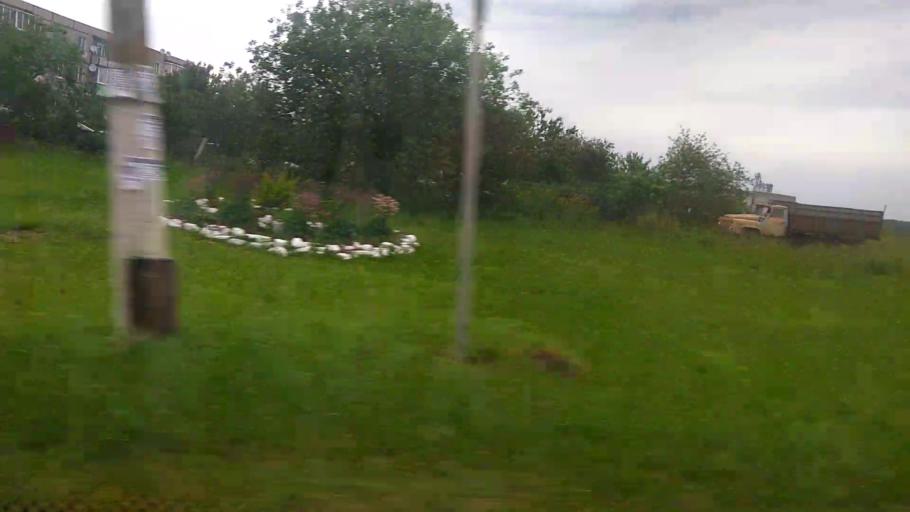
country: RU
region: Moskovskaya
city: Ozery
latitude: 54.7710
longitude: 38.6442
